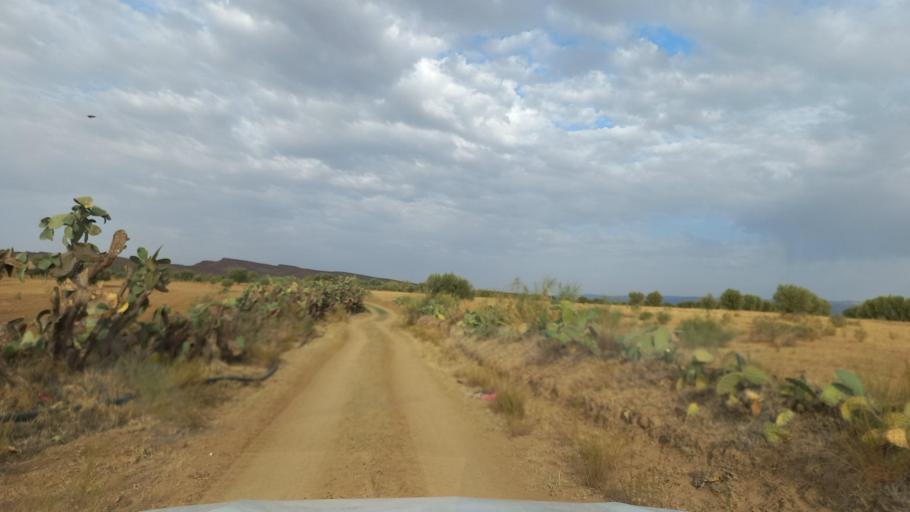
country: TN
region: Al Qasrayn
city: Kasserine
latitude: 35.1880
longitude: 9.0526
